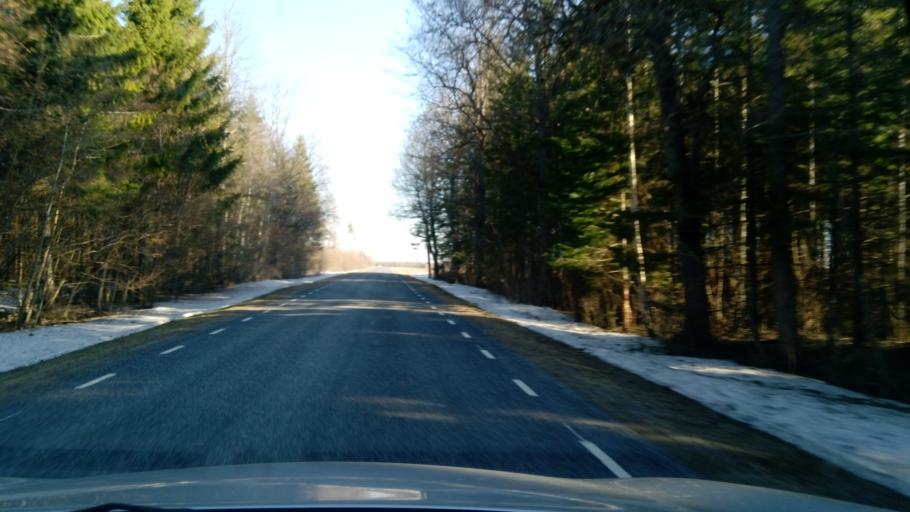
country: EE
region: Laeaene-Virumaa
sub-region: Tamsalu vald
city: Tamsalu
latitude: 59.1997
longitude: 26.1340
